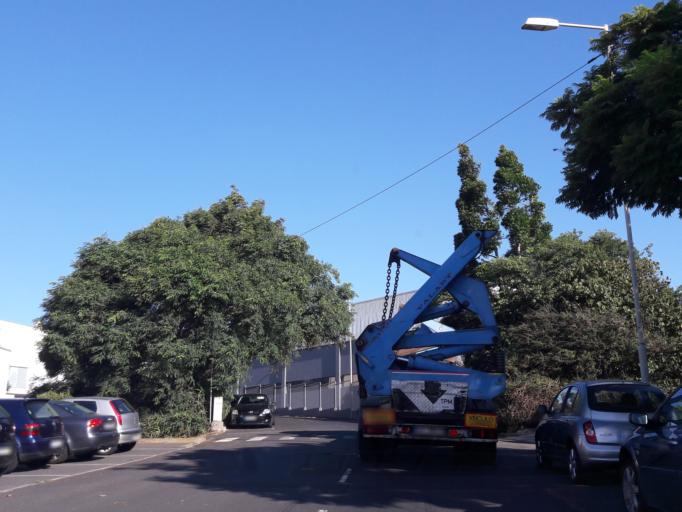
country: PT
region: Madeira
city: Canico
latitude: 32.6513
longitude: -16.8592
